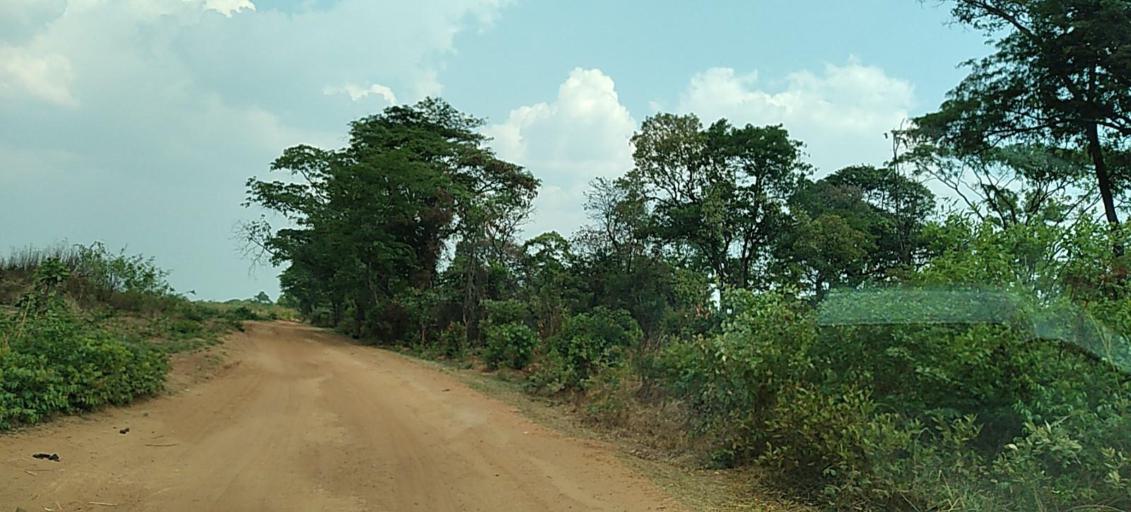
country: ZM
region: Copperbelt
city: Chingola
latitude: -12.7467
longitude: 27.7802
